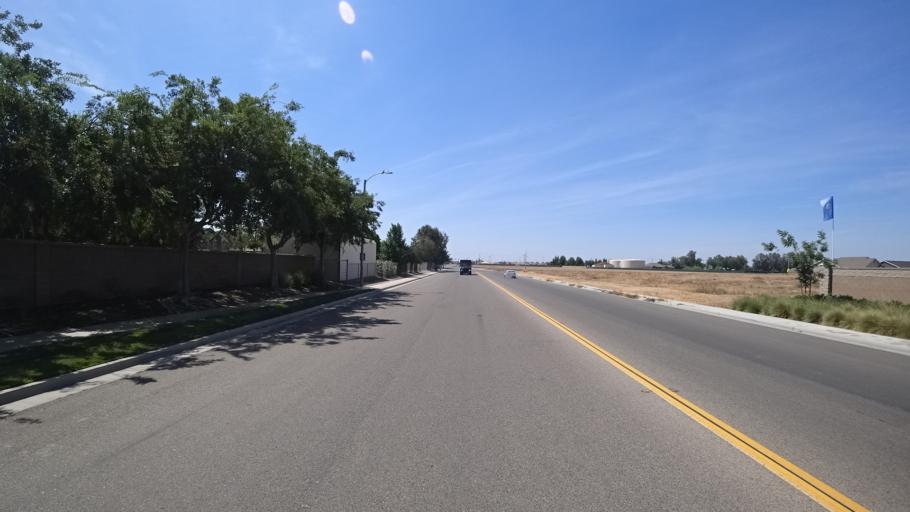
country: US
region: California
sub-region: Kings County
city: Lucerne
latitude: 36.3465
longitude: -119.6821
